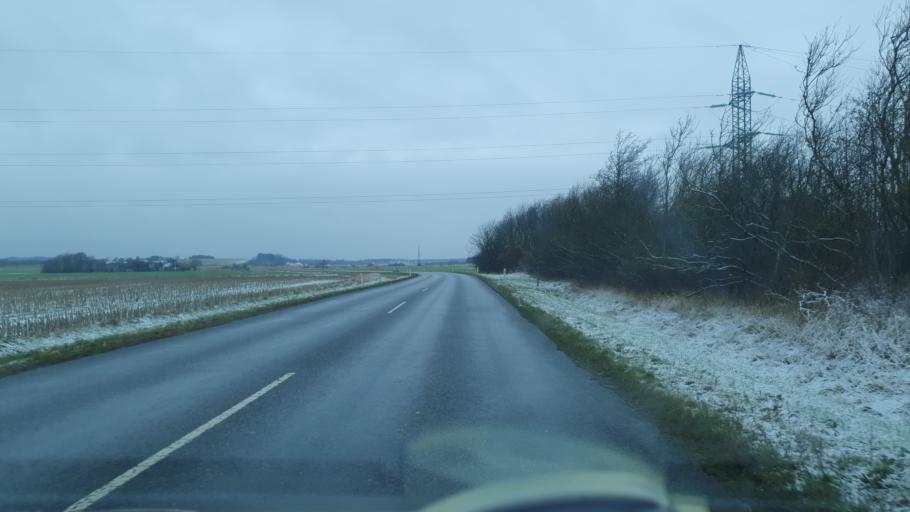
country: DK
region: North Denmark
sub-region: Jammerbugt Kommune
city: Brovst
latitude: 57.1137
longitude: 9.5007
